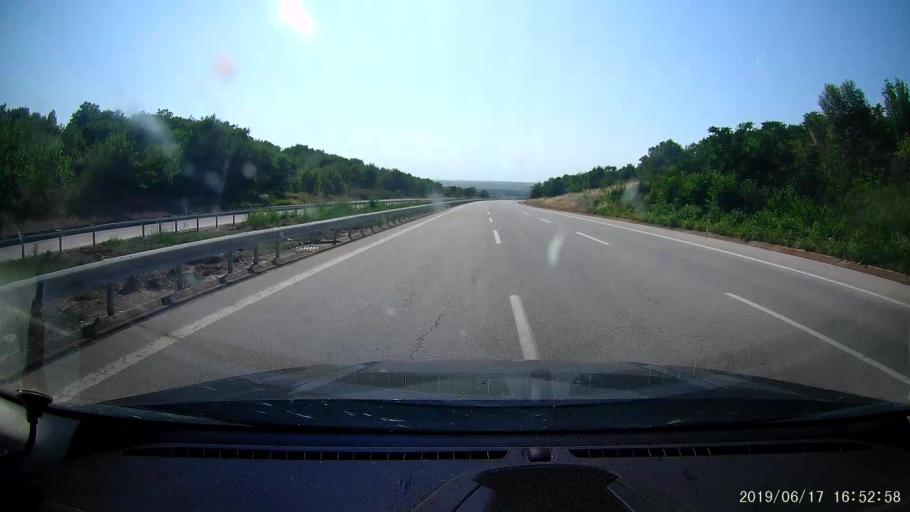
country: TR
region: Kirklareli
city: Inece
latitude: 41.5597
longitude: 27.0369
